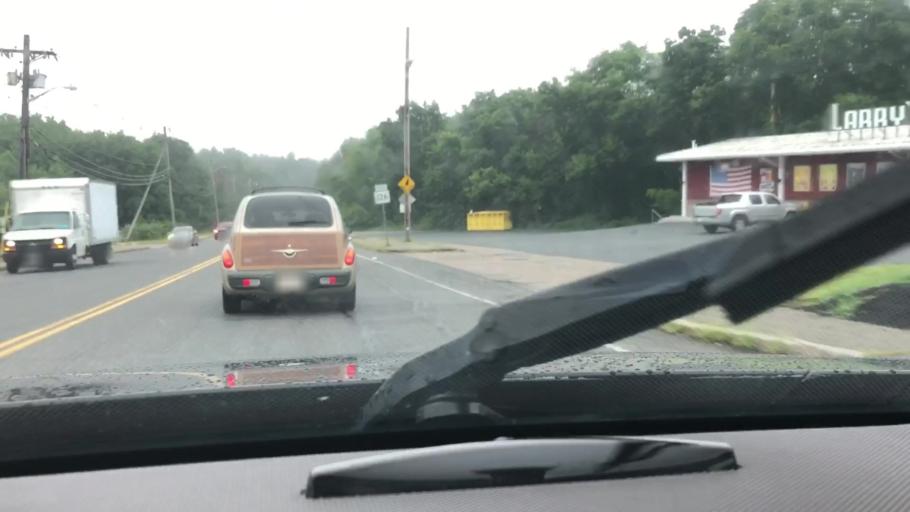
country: US
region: Massachusetts
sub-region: Norfolk County
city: Bellingham
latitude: 42.1134
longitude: -71.4728
